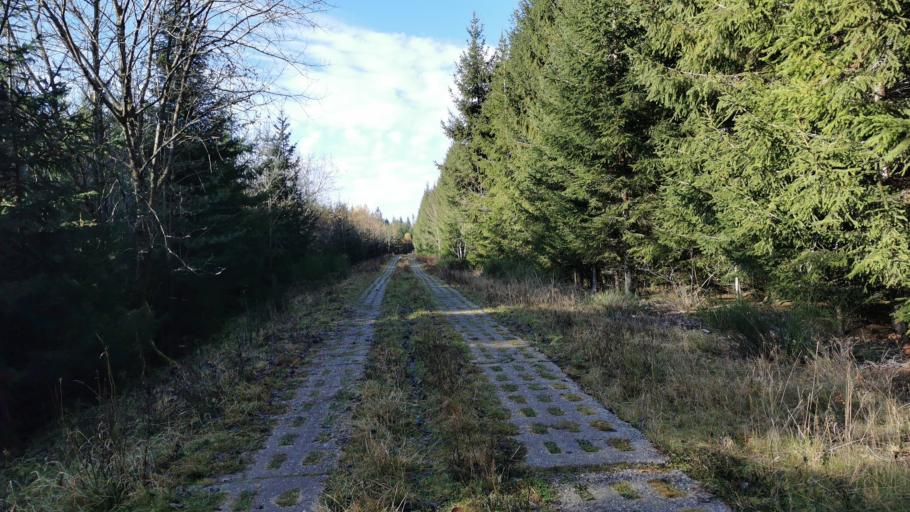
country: DE
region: Bavaria
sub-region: Upper Franconia
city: Reichenbach
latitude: 50.4406
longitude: 11.4325
